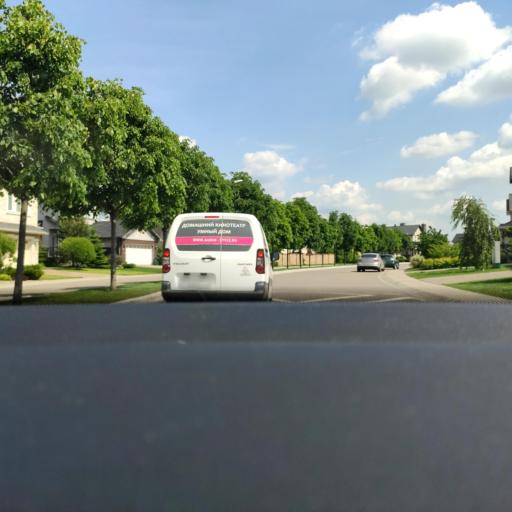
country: RU
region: Moscow
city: Lianozovo
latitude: 55.9286
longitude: 37.6013
